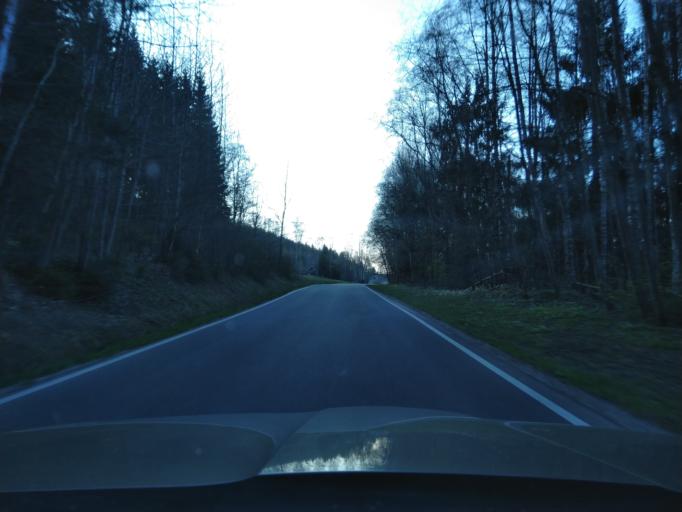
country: CZ
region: Jihocesky
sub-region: Okres Prachatice
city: Vimperk
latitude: 48.9507
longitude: 13.7834
